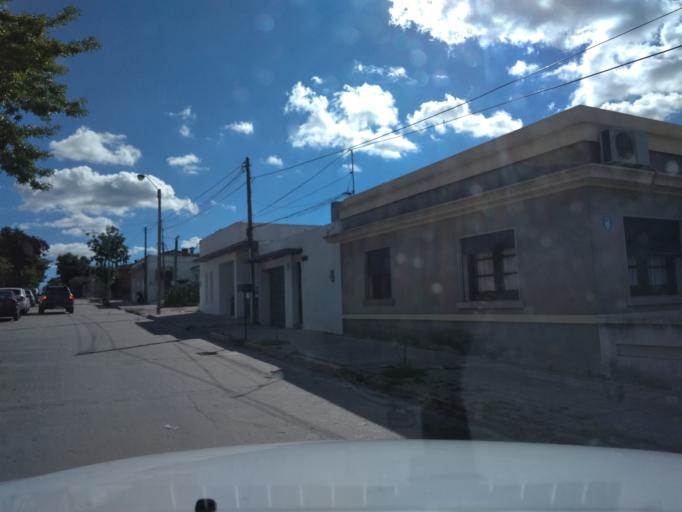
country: UY
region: Florida
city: Florida
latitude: -34.0946
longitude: -56.2126
